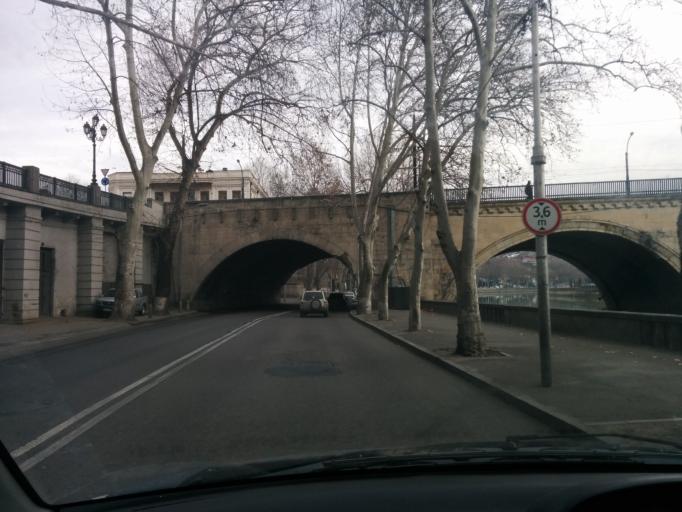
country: GE
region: T'bilisi
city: Tbilisi
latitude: 41.7027
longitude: 44.8038
